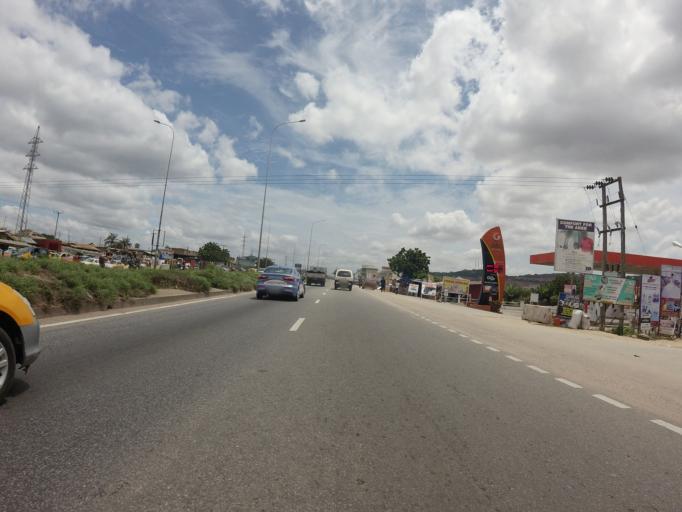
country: GH
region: Central
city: Kasoa
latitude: 5.5391
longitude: -0.3982
